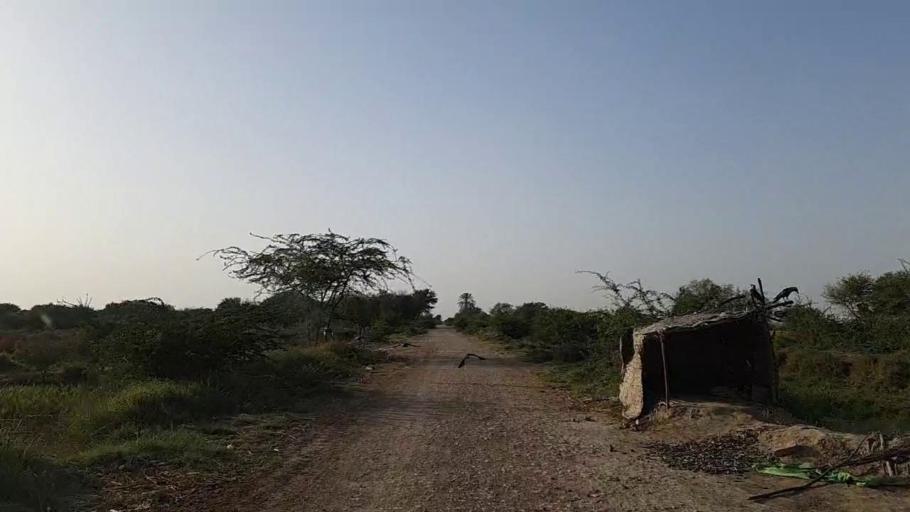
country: PK
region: Sindh
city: Jati
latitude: 24.3444
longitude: 68.1444
